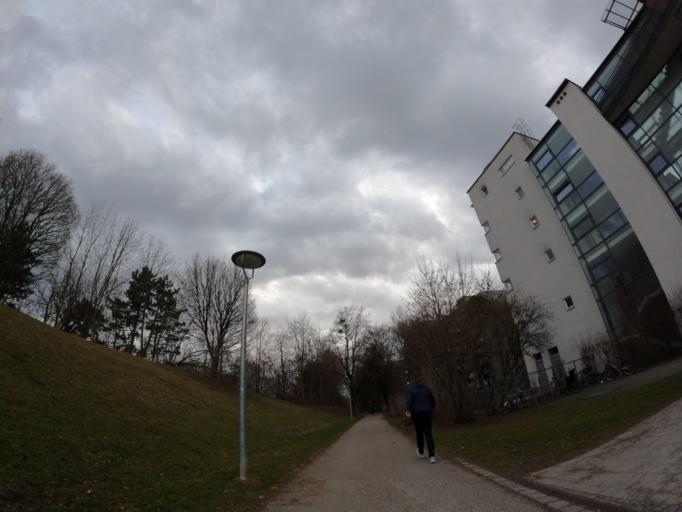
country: DE
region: Bavaria
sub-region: Upper Bavaria
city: Unterhaching
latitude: 48.1086
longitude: 11.6138
